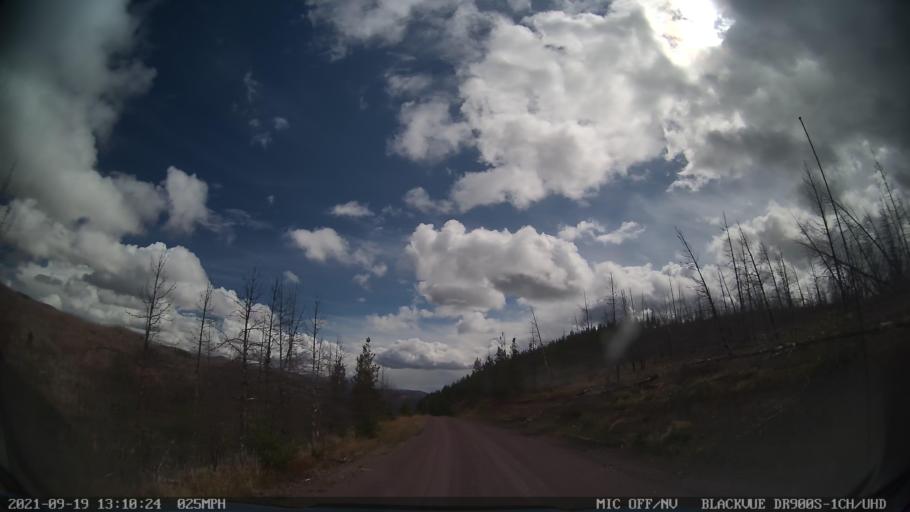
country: US
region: Montana
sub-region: Missoula County
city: Seeley Lake
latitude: 47.1783
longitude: -113.3524
